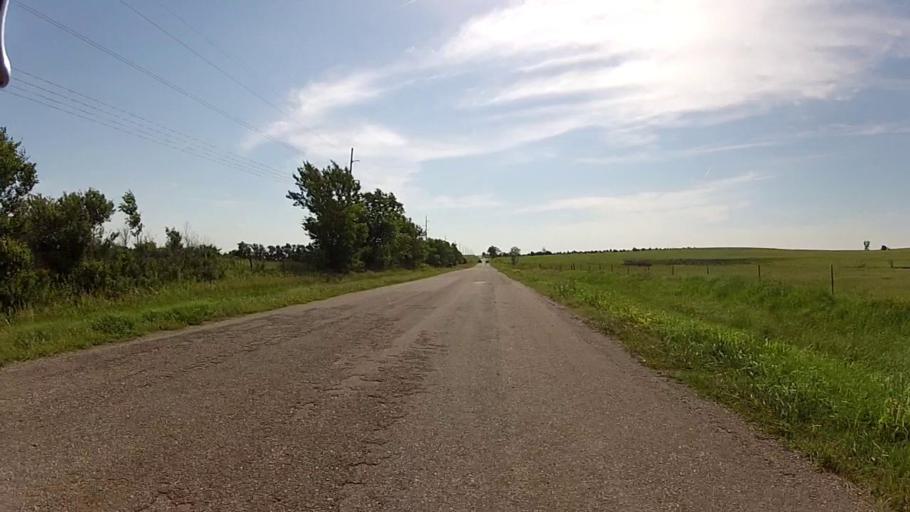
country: US
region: Kansas
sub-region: Cowley County
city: Winfield
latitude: 37.0710
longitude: -96.6600
